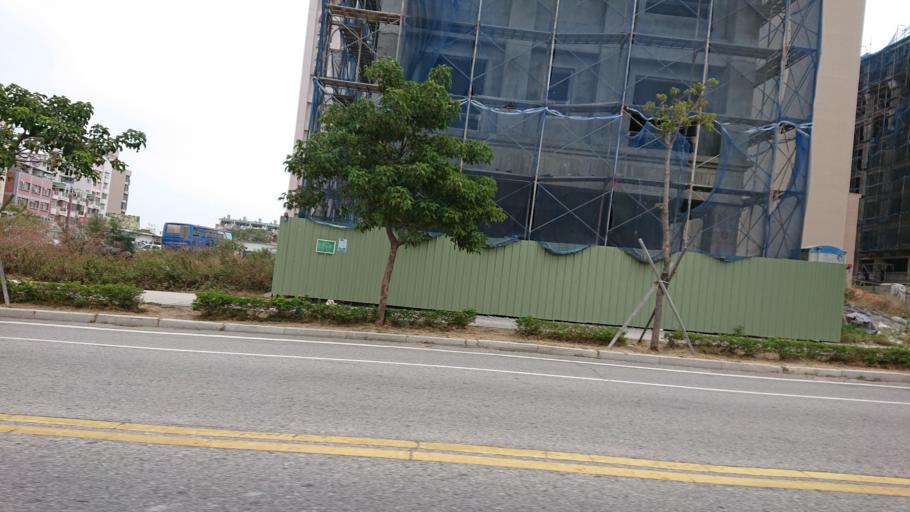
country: TW
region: Fukien
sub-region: Kinmen
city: Jincheng
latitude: 24.4393
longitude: 118.4122
